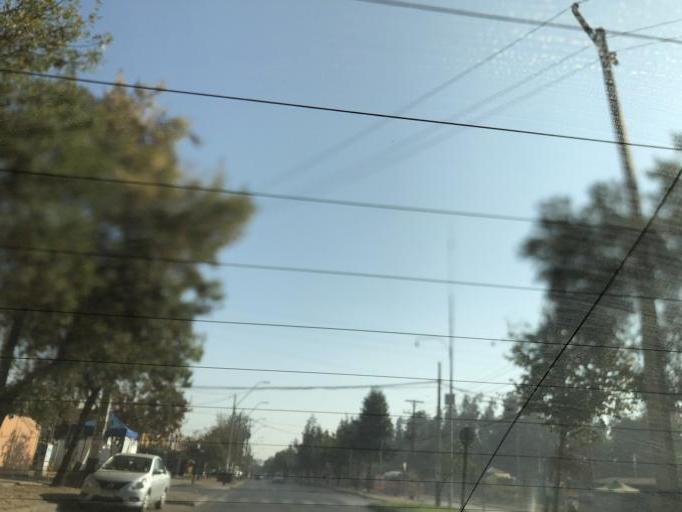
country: CL
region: Santiago Metropolitan
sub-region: Provincia de Cordillera
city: Puente Alto
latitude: -33.6101
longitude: -70.5547
